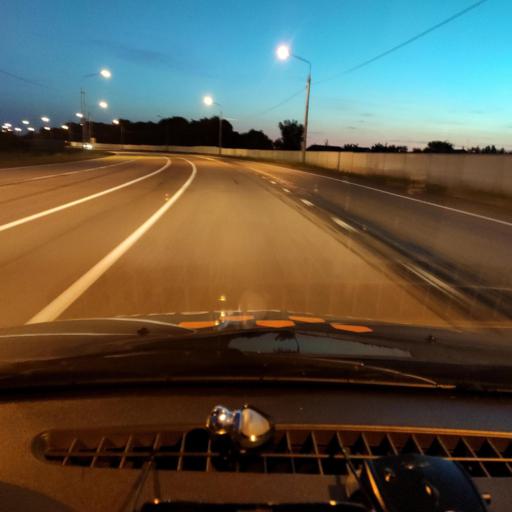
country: RU
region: Belgorod
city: Skorodnoye
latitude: 51.1868
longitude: 37.3674
